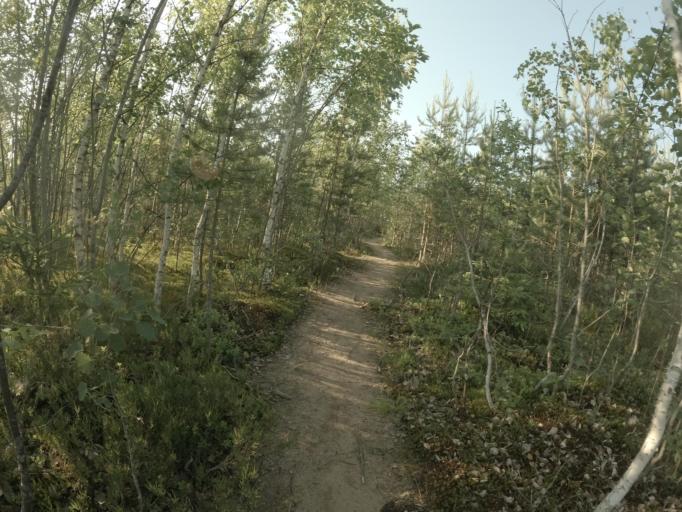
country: RU
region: Leningrad
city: Yakovlevo
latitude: 60.4421
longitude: 29.2402
